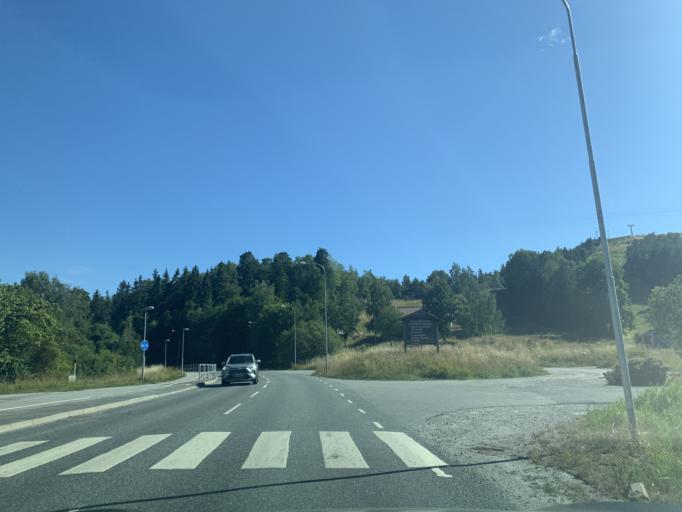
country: SE
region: Stockholm
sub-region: Ekero Kommun
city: Ekeroe
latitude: 59.2814
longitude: 17.8344
